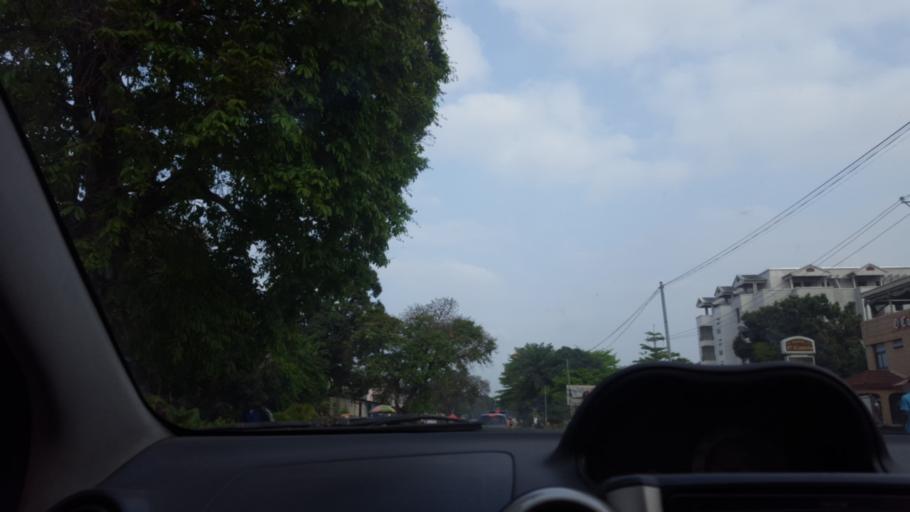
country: CD
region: Kinshasa
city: Kinshasa
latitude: -4.3239
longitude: 15.2818
